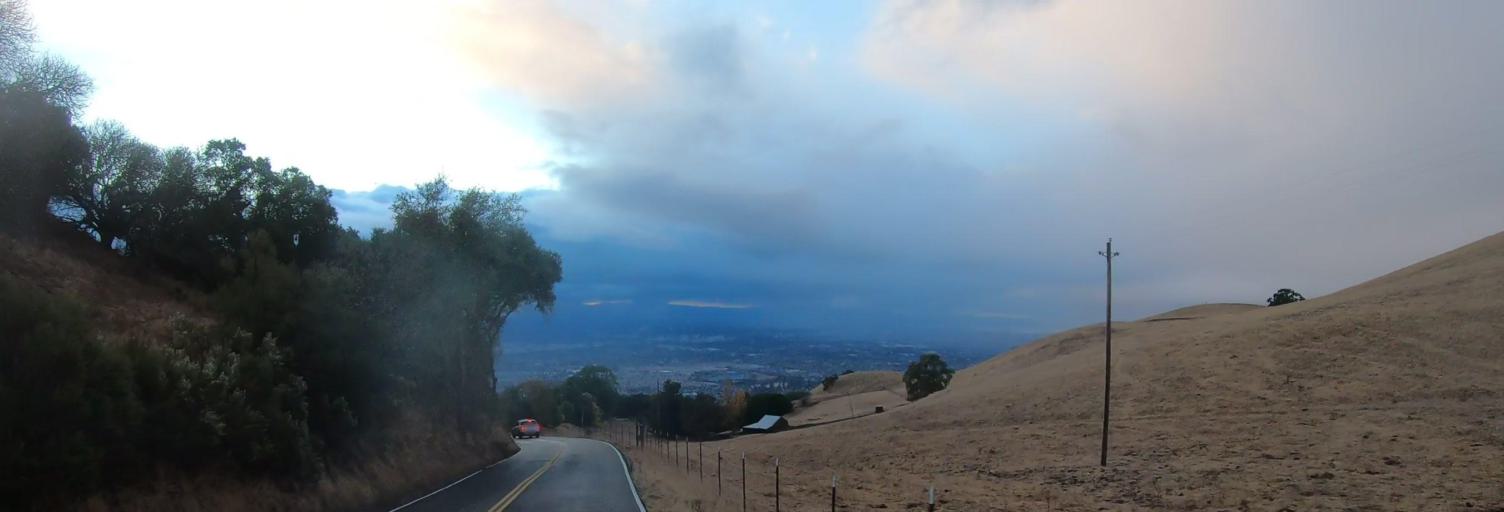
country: US
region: California
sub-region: Santa Clara County
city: East Foothills
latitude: 37.3322
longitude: -121.7380
